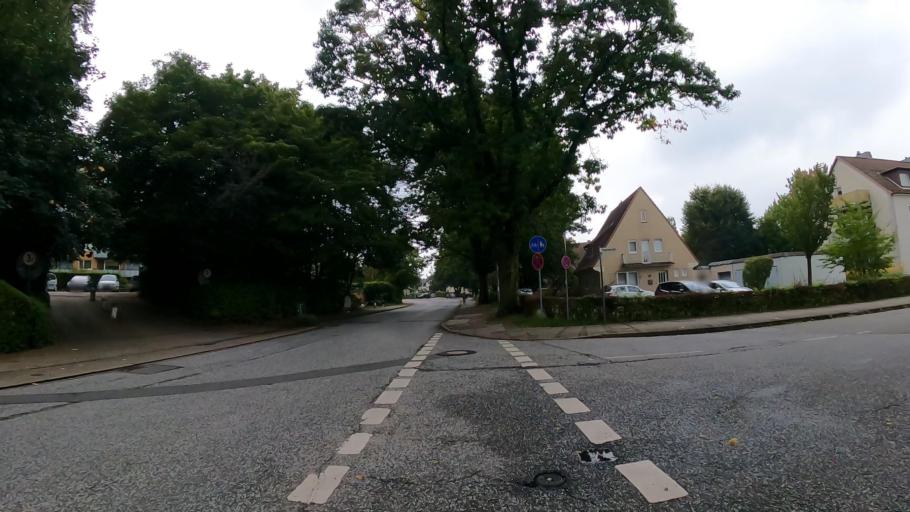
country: DE
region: Schleswig-Holstein
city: Halstenbek
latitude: 53.6278
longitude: 9.8367
